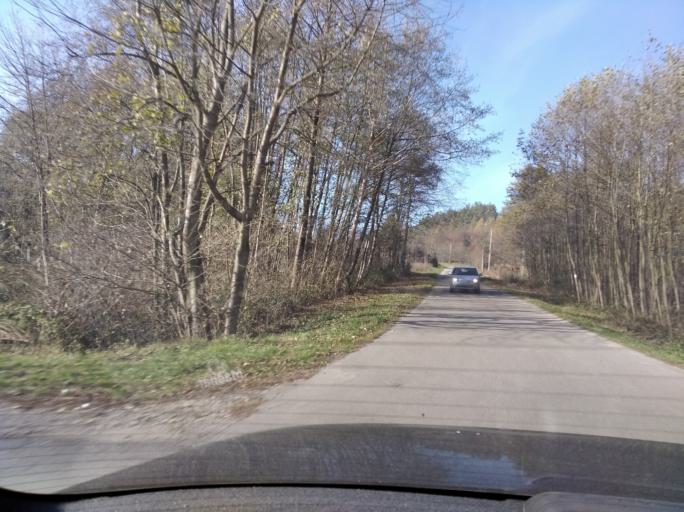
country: PL
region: Subcarpathian Voivodeship
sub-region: Powiat ropczycko-sedziszowski
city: Wielopole Skrzynskie
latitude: 49.8942
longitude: 21.6009
